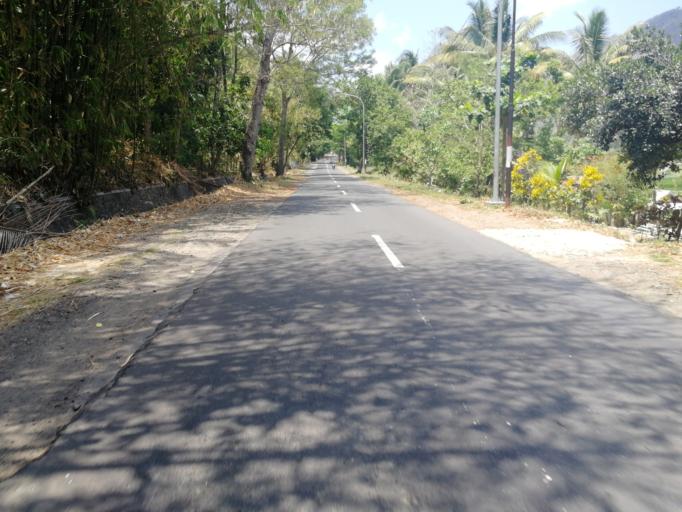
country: ID
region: West Nusa Tenggara
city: Karangsubagan
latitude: -8.4190
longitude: 116.0958
